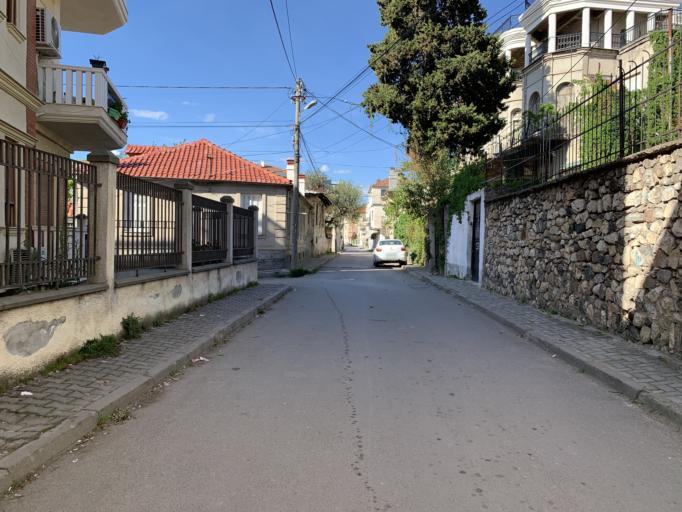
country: AL
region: Korce
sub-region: Rrethi i Korces
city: Korce
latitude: 40.6177
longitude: 20.7838
